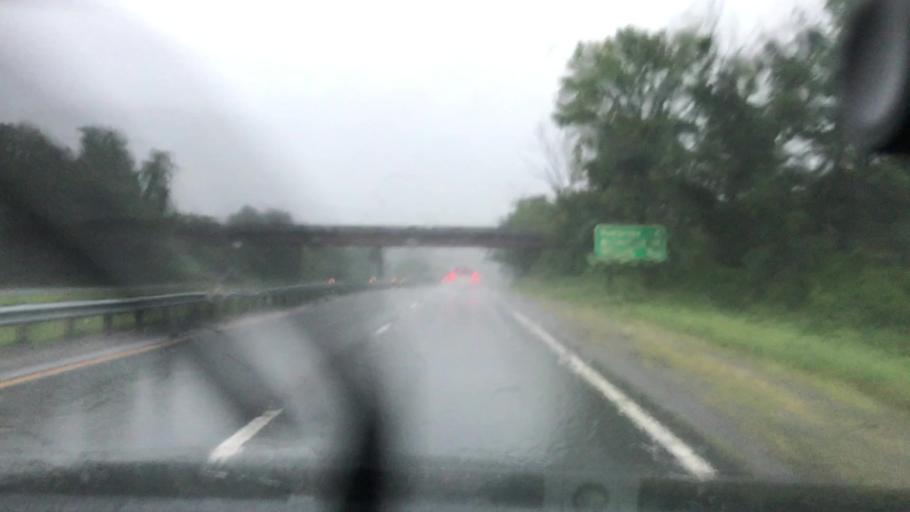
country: US
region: Virginia
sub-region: Giles County
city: Pearisburg
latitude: 37.3382
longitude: -80.7281
